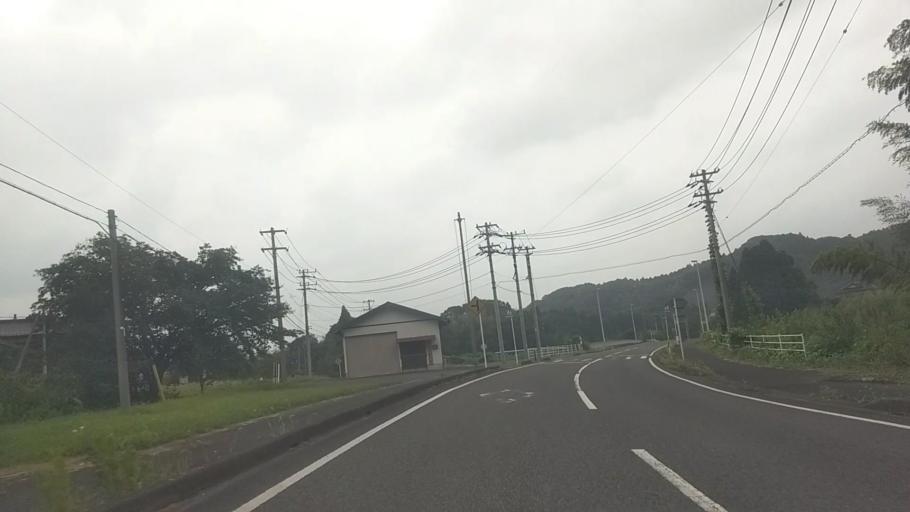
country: JP
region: Chiba
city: Ohara
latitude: 35.2662
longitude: 140.2543
